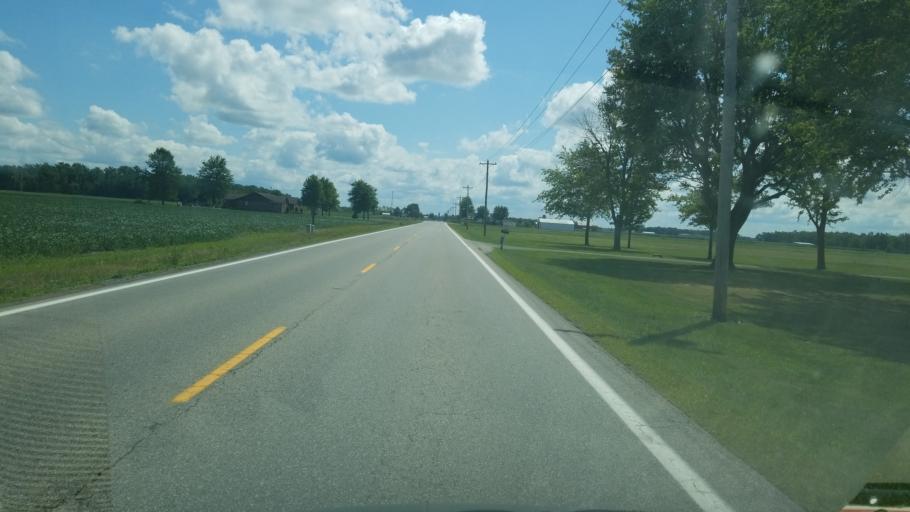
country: US
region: Ohio
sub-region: Putnam County
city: Kalida
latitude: 41.0229
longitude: -84.1981
